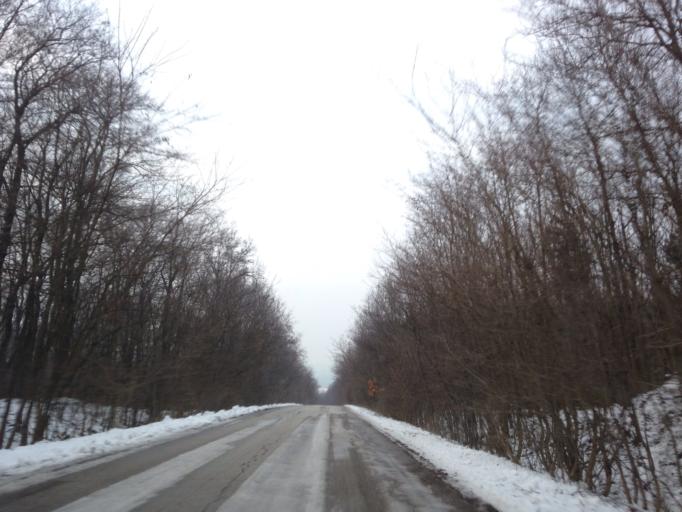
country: SK
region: Nitriansky
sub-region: Okres Nitra
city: Vrable
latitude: 48.0961
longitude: 18.3644
